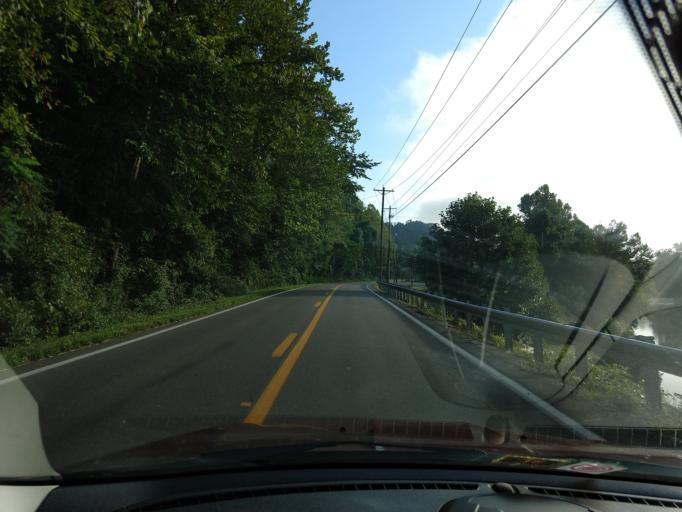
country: US
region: West Virginia
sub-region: Kanawha County
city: Charleston
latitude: 38.3830
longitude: -81.5961
